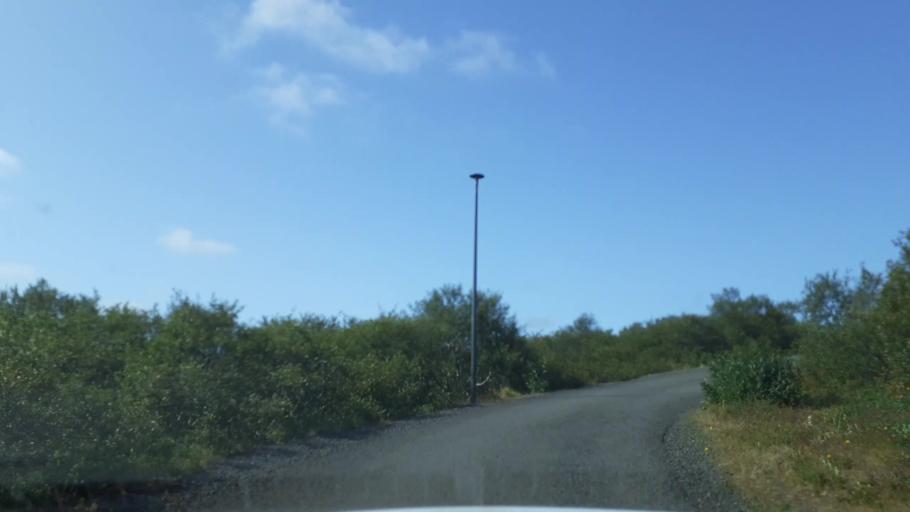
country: IS
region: West
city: Borgarnes
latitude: 64.7009
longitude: -21.6171
